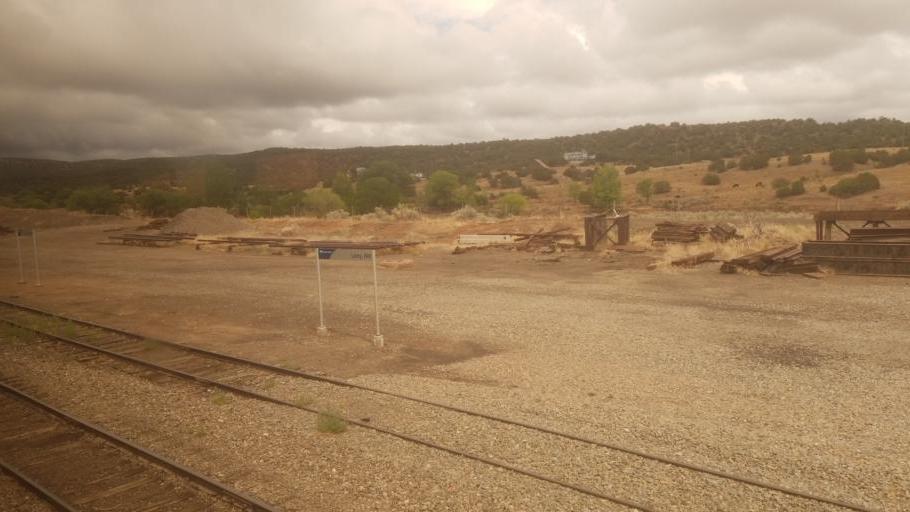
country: US
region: New Mexico
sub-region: Santa Fe County
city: Eldorado at Santa Fe
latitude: 35.4807
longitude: -105.8801
